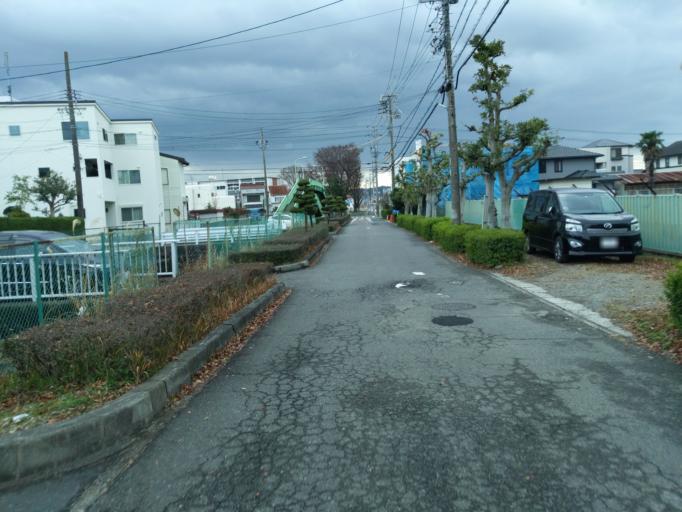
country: JP
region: Aichi
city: Kasugai
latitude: 35.2563
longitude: 136.9888
